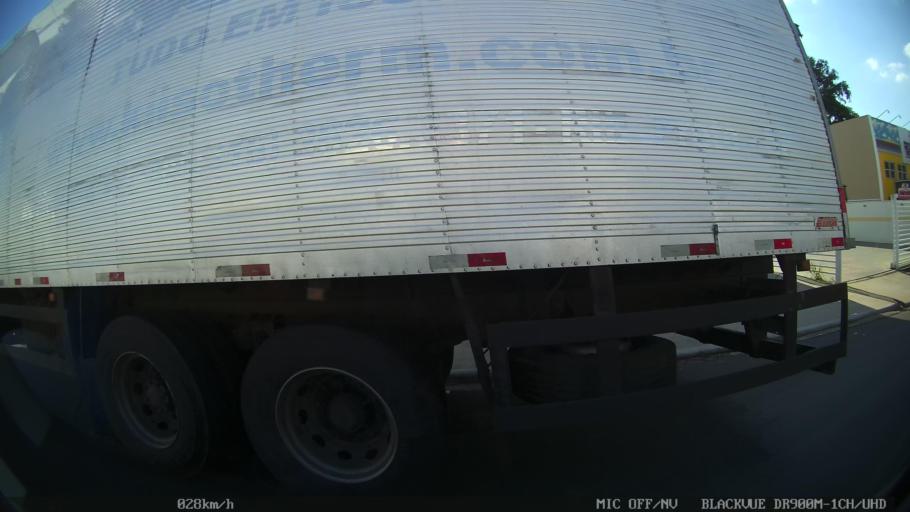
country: BR
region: Sao Paulo
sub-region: Nova Odessa
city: Nova Odessa
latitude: -22.7870
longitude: -47.3021
